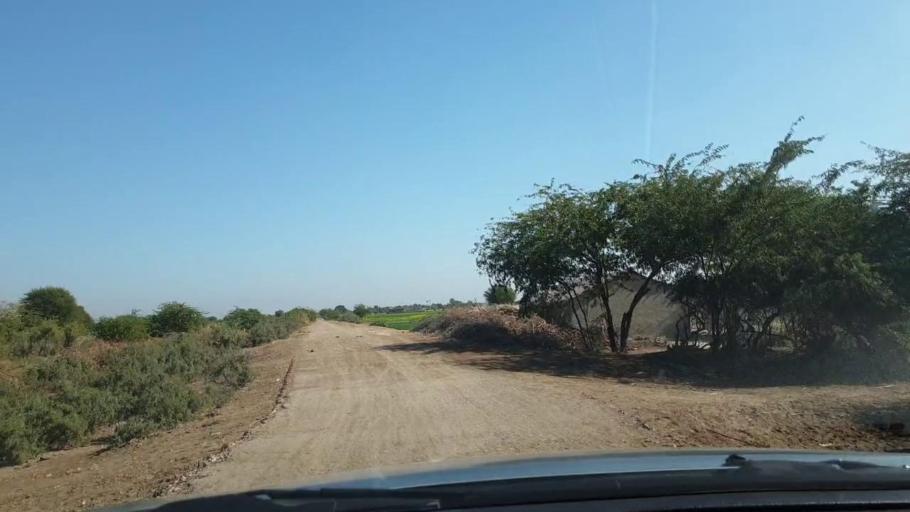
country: PK
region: Sindh
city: Jhol
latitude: 25.9212
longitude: 68.9519
